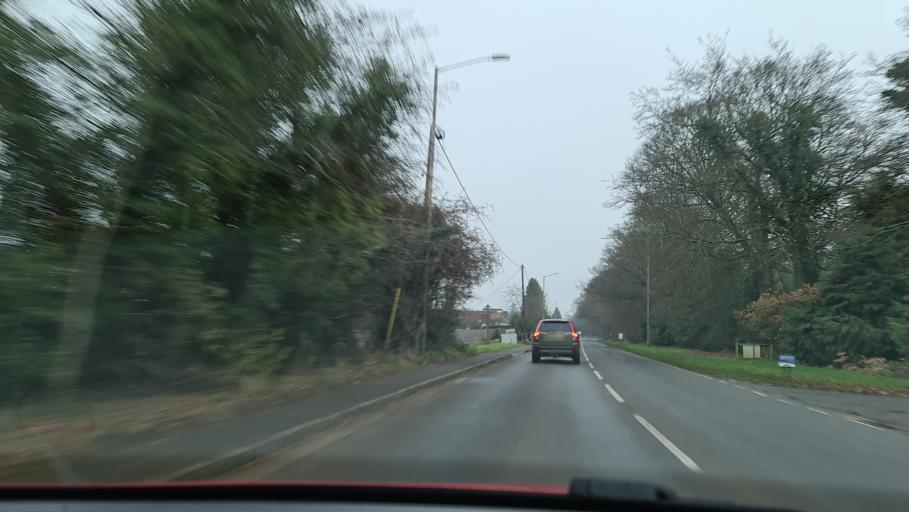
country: GB
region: England
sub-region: Buckinghamshire
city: Stokenchurch
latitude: 51.6521
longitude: -0.8685
